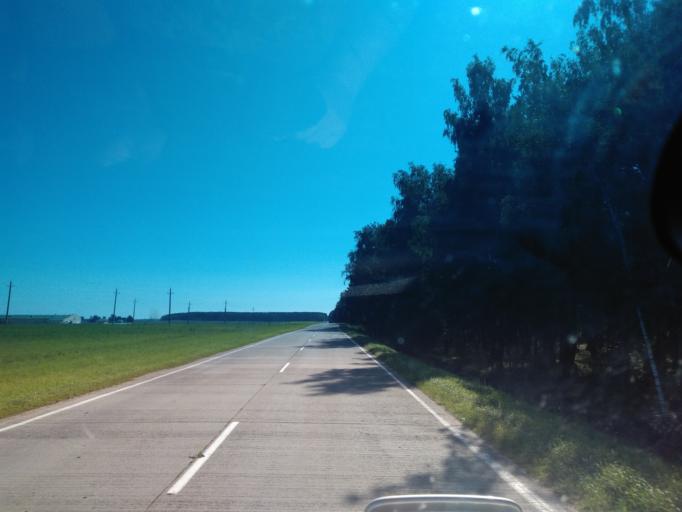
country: BY
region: Minsk
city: Stan'kava
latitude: 53.6256
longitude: 27.2695
